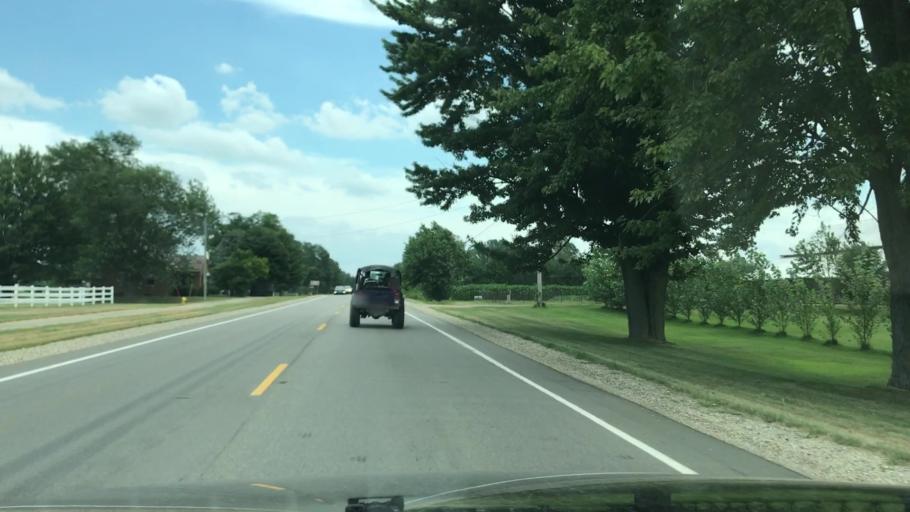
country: US
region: Michigan
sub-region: Ottawa County
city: Zeeland
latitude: 42.7833
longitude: -85.9898
